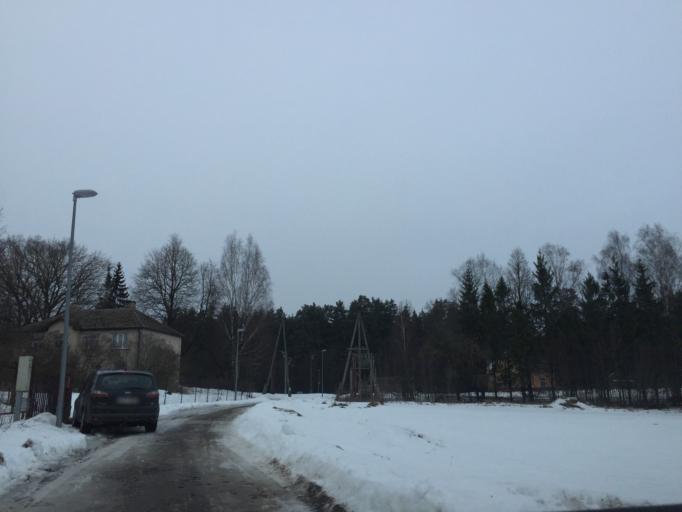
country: LV
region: Ikskile
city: Ikskile
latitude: 56.8485
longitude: 24.4361
